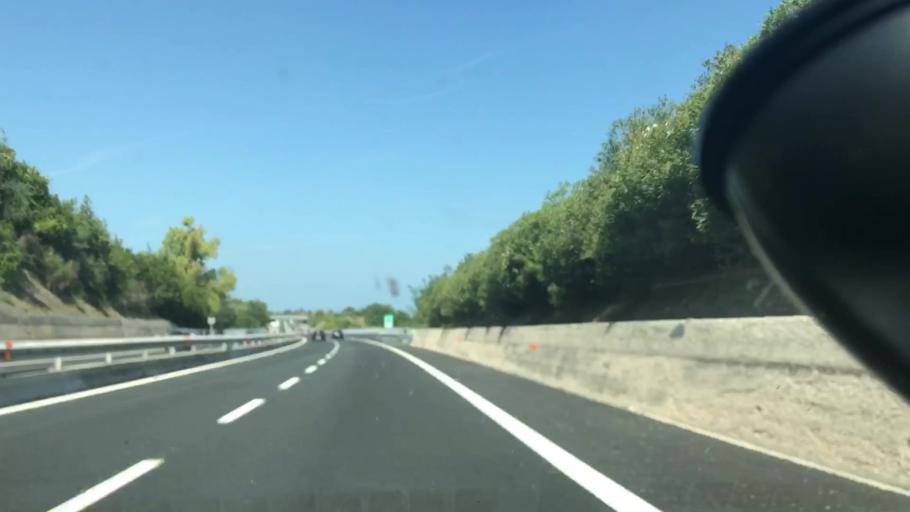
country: IT
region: Abruzzo
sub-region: Provincia di Chieti
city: Ortona
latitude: 42.3459
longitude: 14.3570
